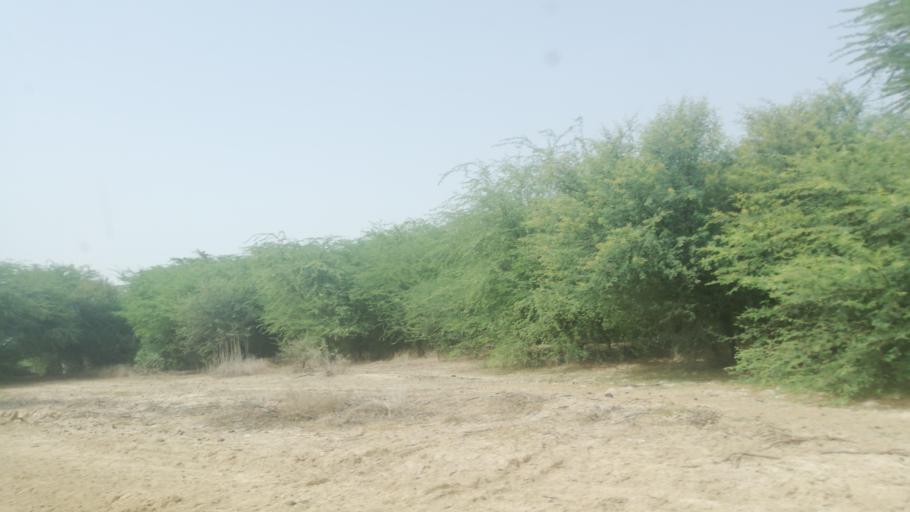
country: SN
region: Saint-Louis
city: Saint-Louis
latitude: 16.0607
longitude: -16.3117
